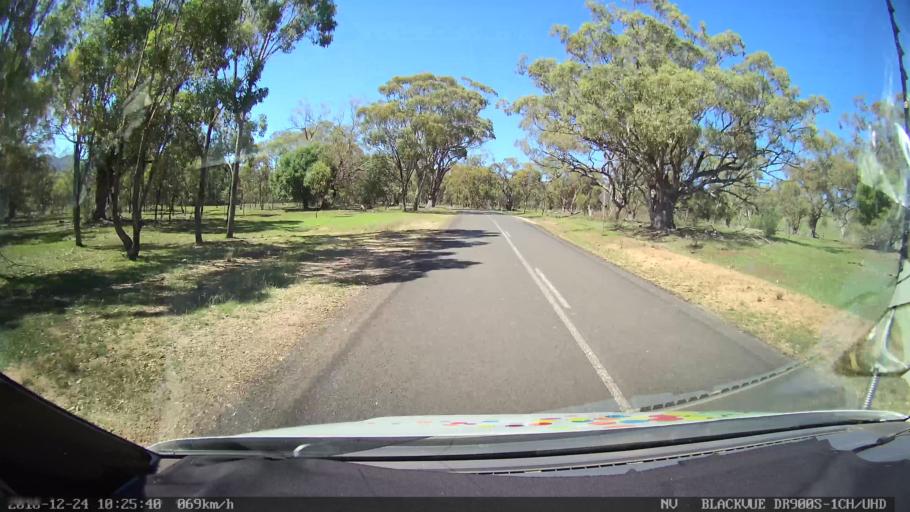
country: AU
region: New South Wales
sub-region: Liverpool Plains
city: Quirindi
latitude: -31.8015
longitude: 150.5276
